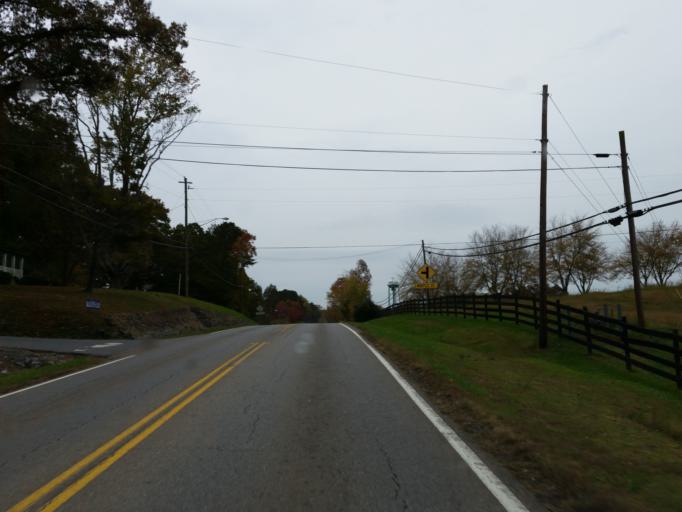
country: US
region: Georgia
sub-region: Pickens County
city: Jasper
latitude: 34.4659
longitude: -84.4408
